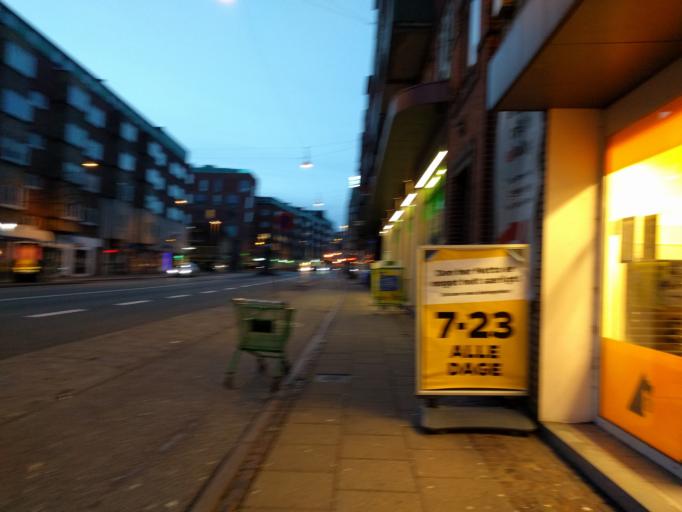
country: DK
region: North Denmark
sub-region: Alborg Kommune
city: Aalborg
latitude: 57.0503
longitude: 9.9164
